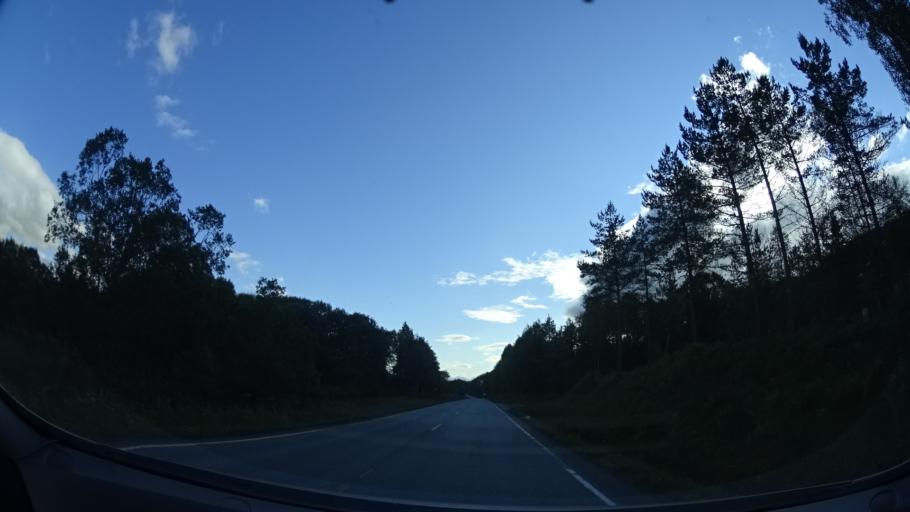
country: NO
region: More og Romsdal
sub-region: Molde
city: Hjelset
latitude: 62.7929
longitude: 7.5370
